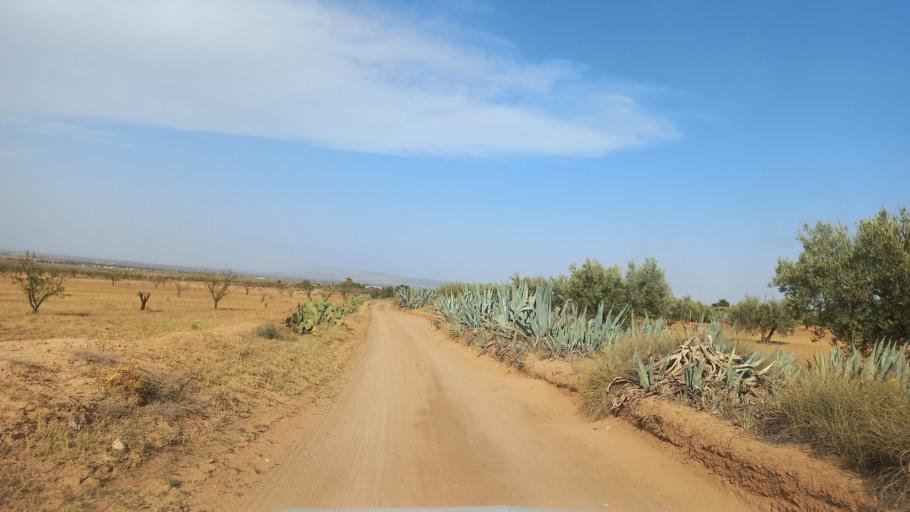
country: TN
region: Al Qasrayn
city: Kasserine
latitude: 35.2085
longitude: 8.9673
